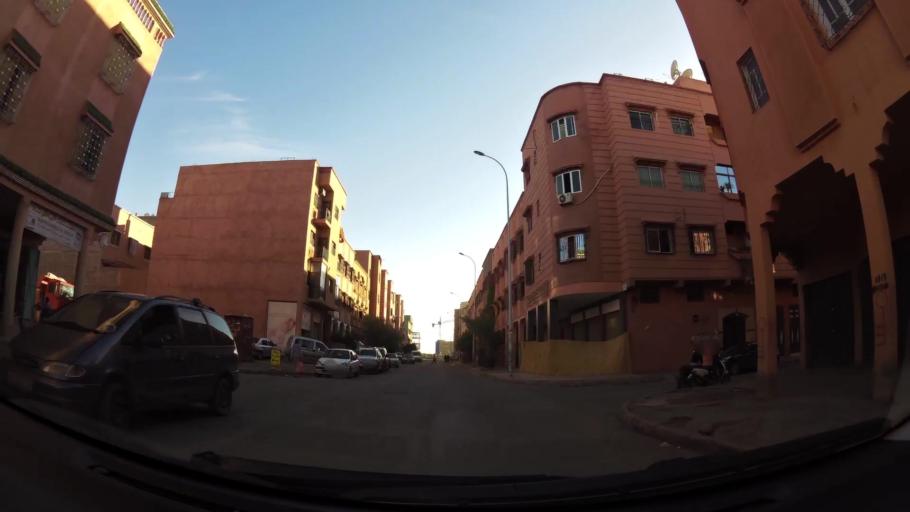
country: MA
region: Marrakech-Tensift-Al Haouz
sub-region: Marrakech
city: Marrakesh
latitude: 31.6166
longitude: -8.0638
